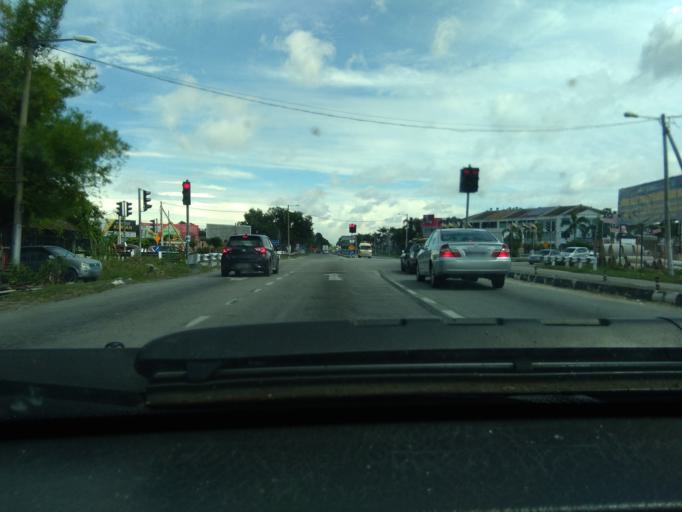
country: MY
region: Perak
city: Parit Buntar
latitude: 5.1106
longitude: 100.4823
